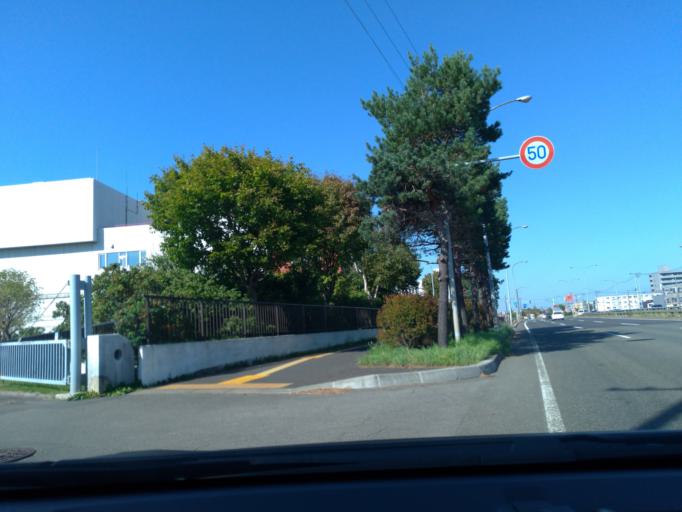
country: JP
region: Hokkaido
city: Sapporo
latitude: 43.1135
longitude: 141.3435
